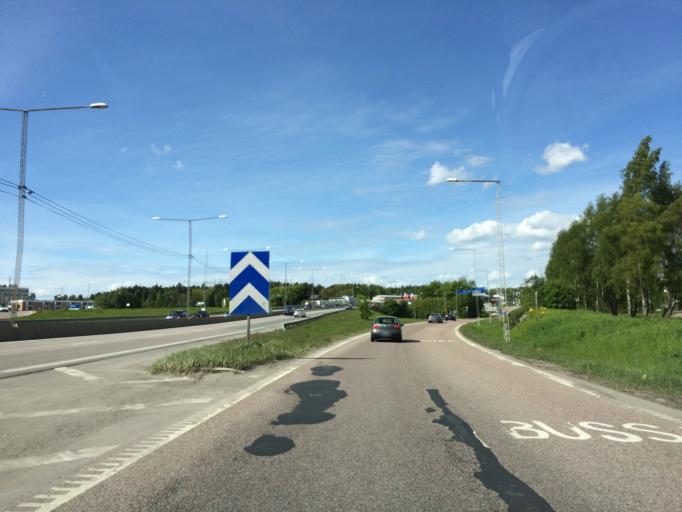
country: SE
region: Stockholm
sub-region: Danderyds Kommun
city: Djursholm
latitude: 59.4075
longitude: 18.0353
